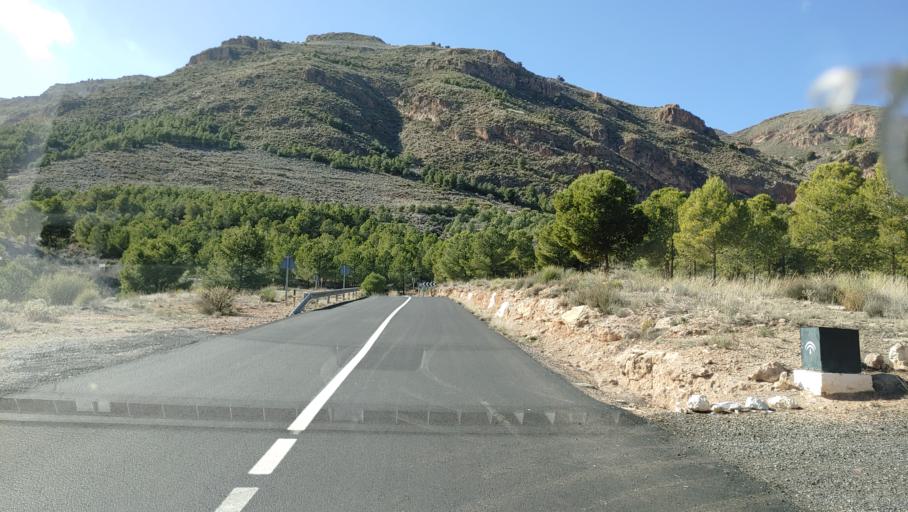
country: ES
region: Andalusia
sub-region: Provincia de Almeria
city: Alicun
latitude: 36.9435
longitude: -2.6022
